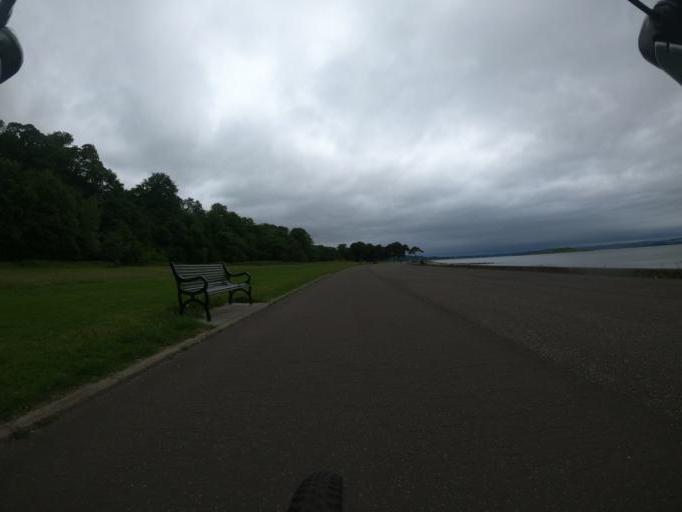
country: GB
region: Scotland
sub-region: Edinburgh
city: Colinton
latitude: 55.9790
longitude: -3.2638
